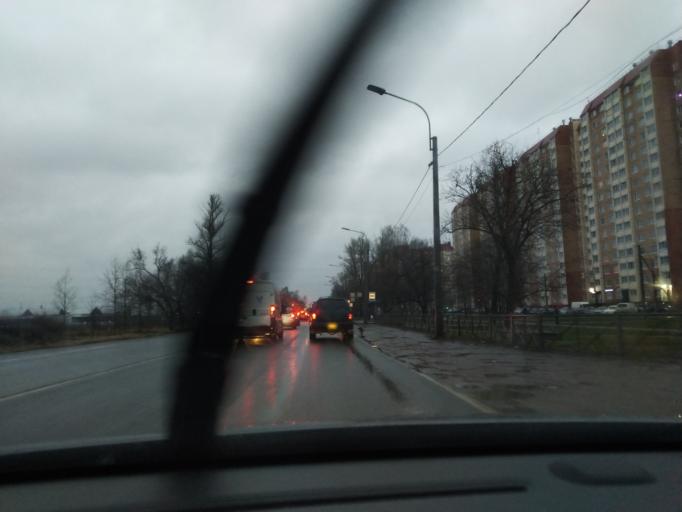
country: RU
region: St.-Petersburg
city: Gorelovo
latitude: 59.7888
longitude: 30.1437
